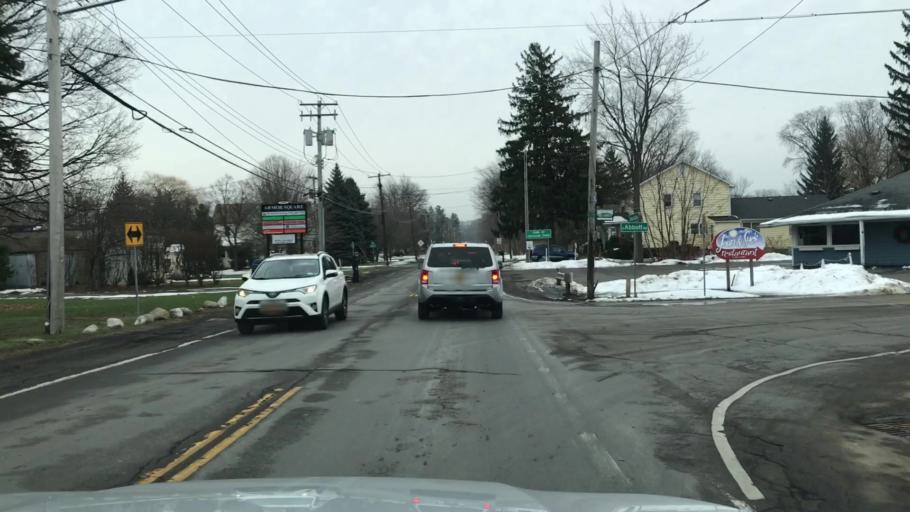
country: US
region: New York
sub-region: Erie County
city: Hamburg
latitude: 42.7404
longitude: -78.7978
